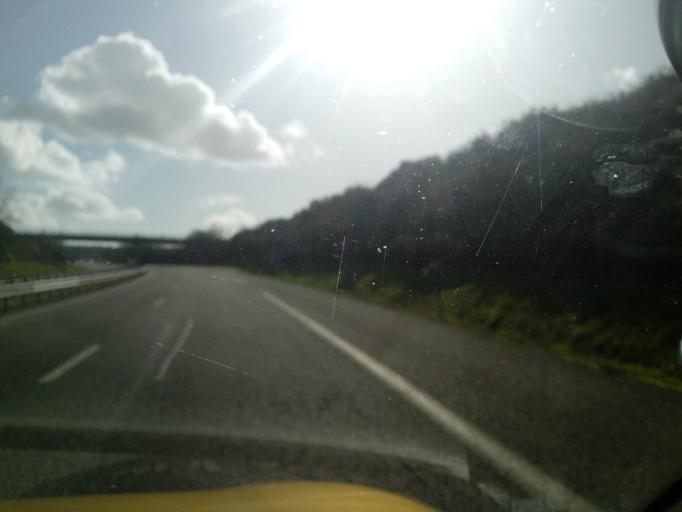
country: FR
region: Brittany
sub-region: Departement du Morbihan
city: Malestroit
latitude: 47.8275
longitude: -2.4331
